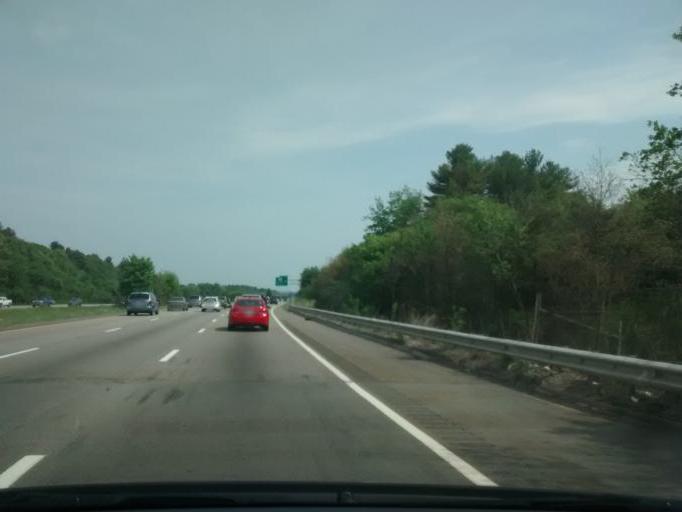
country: US
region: Massachusetts
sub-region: Bristol County
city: Norton Center
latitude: 41.9870
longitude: -71.1654
